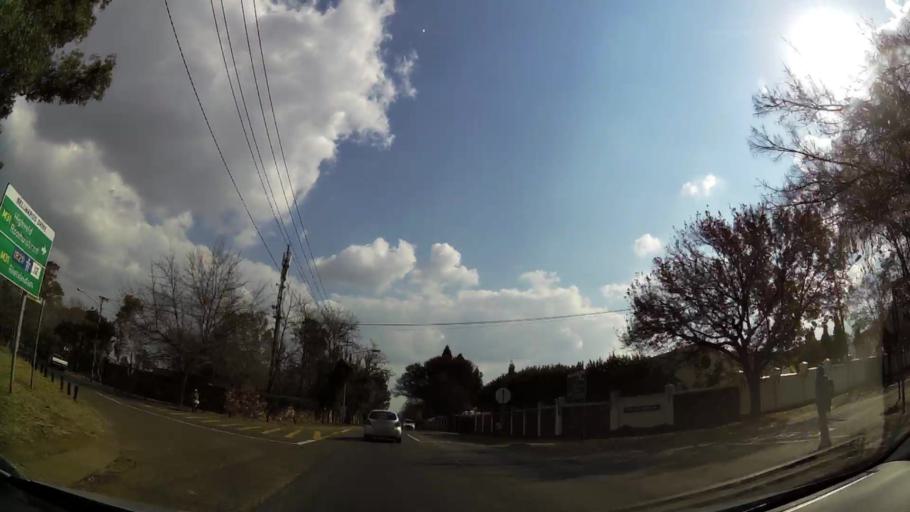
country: ZA
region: Gauteng
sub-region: City of Tshwane Metropolitan Municipality
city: Centurion
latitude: -25.8778
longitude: 28.2195
